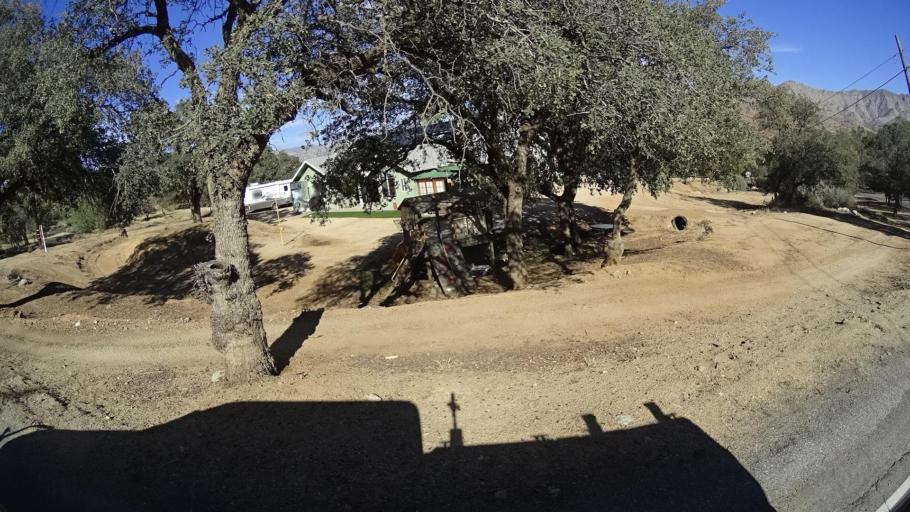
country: US
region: California
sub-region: Kern County
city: Bodfish
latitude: 35.5849
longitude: -118.4985
